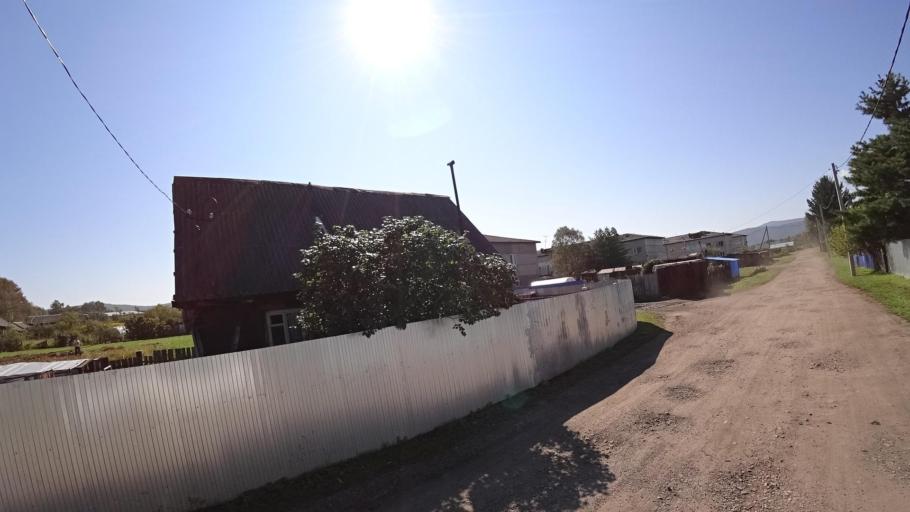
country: RU
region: Jewish Autonomous Oblast
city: Bira
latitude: 48.9990
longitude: 132.4522
